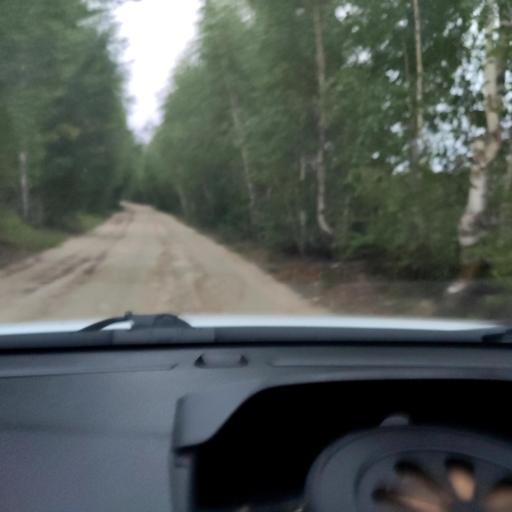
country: RU
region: Tatarstan
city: Vysokaya Gora
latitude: 55.8560
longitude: 49.2505
